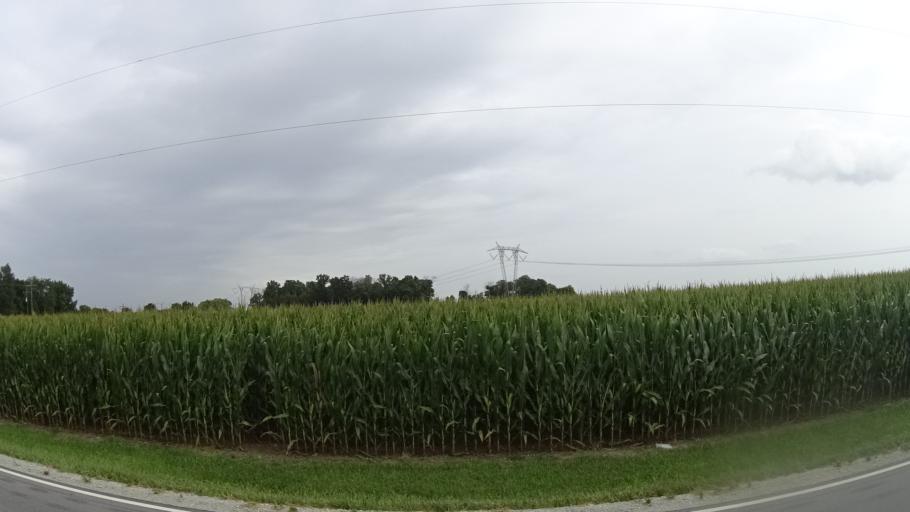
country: US
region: Indiana
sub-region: Madison County
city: Lapel
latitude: 40.0195
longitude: -85.8423
